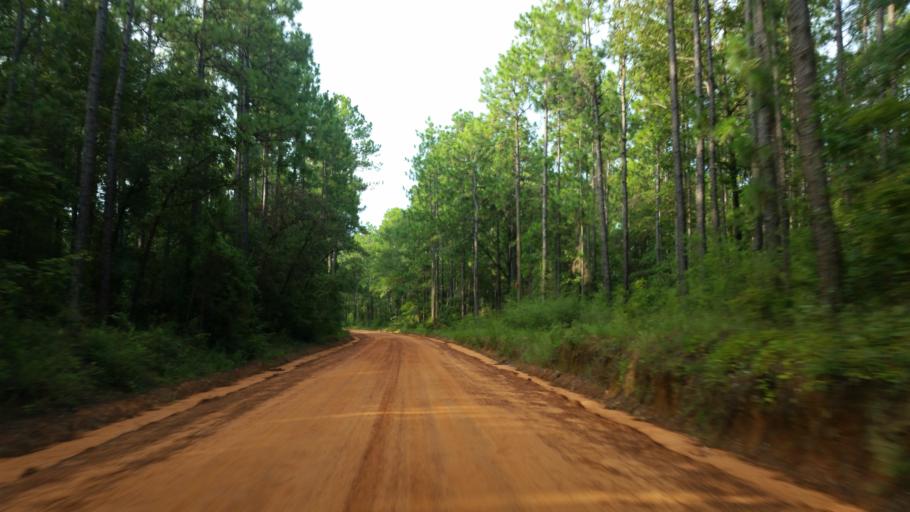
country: US
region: Alabama
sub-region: Escambia County
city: Atmore
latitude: 30.9067
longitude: -87.5833
